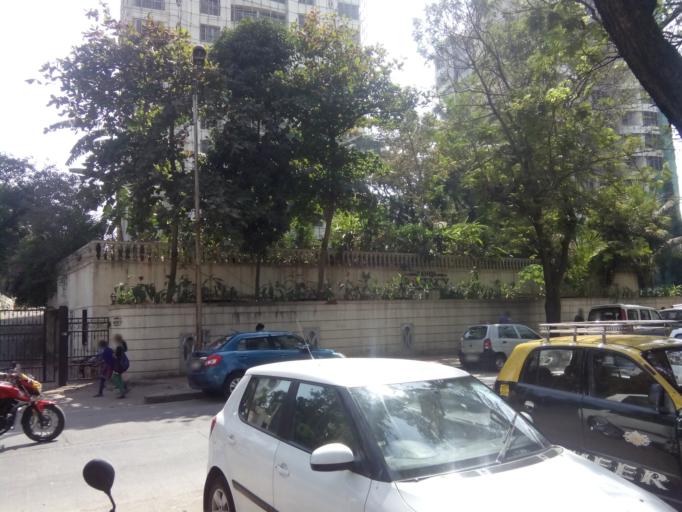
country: IN
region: Maharashtra
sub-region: Mumbai Suburban
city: Mumbai
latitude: 19.0417
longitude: 72.8650
